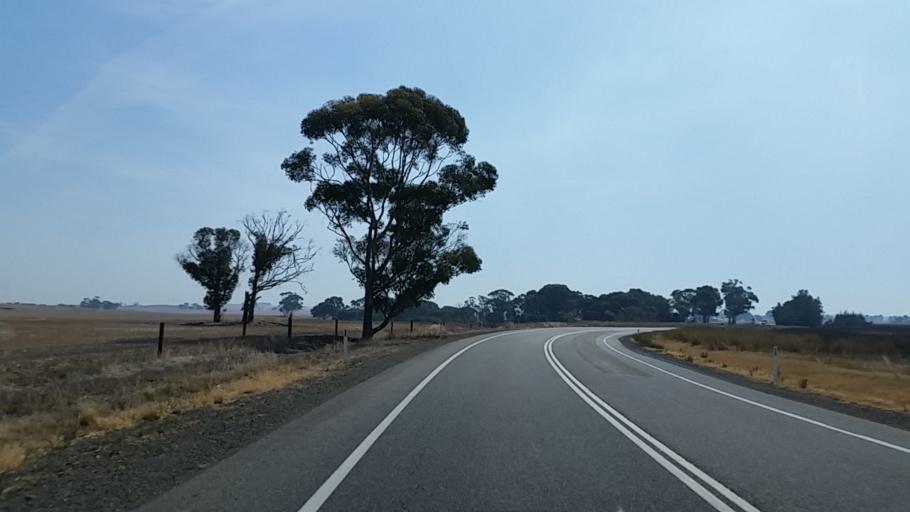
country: AU
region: South Australia
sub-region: Light
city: Kapunda
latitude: -34.2531
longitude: 138.7518
